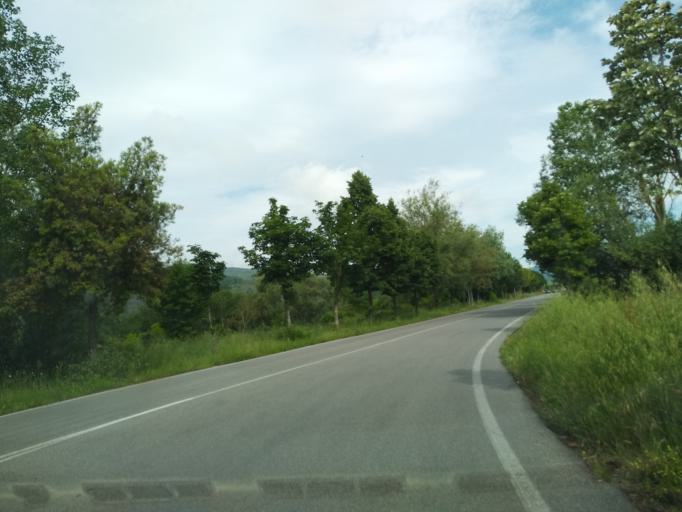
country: IT
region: Tuscany
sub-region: Province of Arezzo
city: Castelnuovo dei Sabbioni
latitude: 43.5589
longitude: 11.4524
